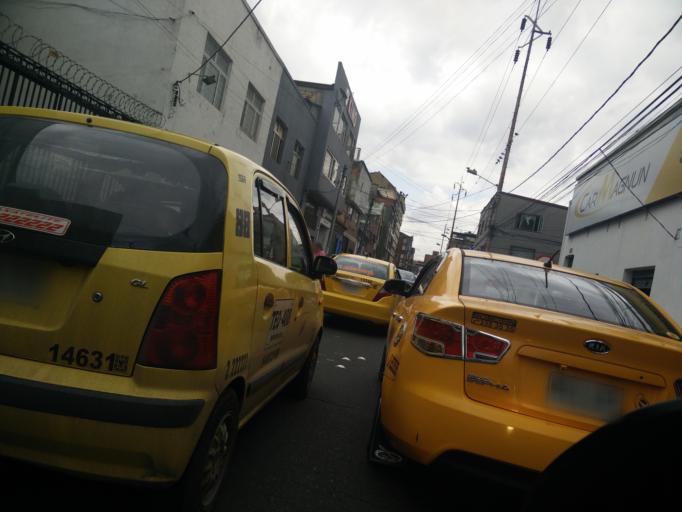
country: CO
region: Bogota D.C.
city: Bogota
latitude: 4.6512
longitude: -74.0655
